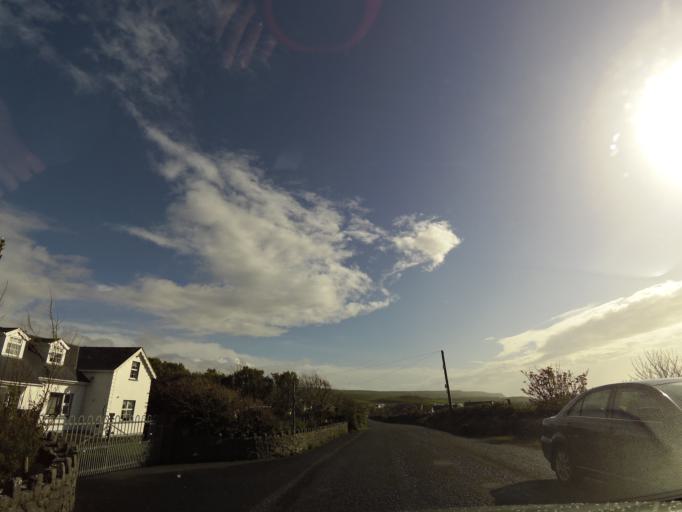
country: IE
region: Connaught
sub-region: County Galway
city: Bearna
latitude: 53.0216
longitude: -9.3694
